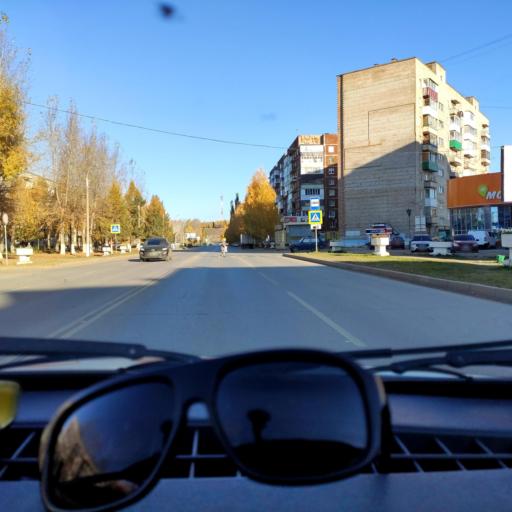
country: RU
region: Bashkortostan
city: Blagoveshchensk
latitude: 55.0497
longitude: 55.9549
